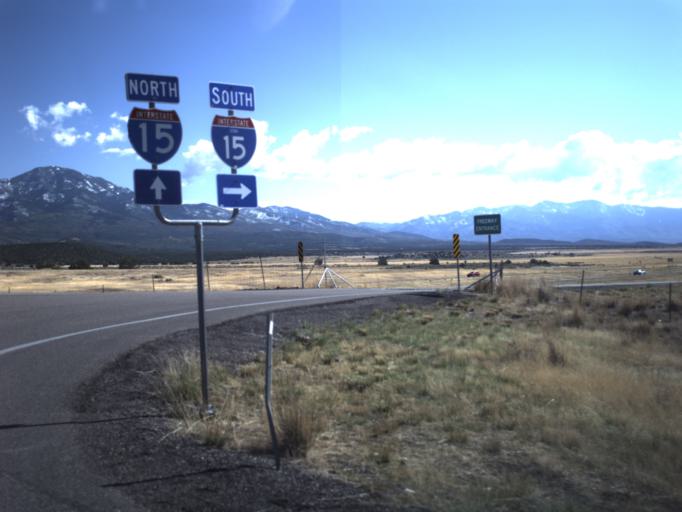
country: US
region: Utah
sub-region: Millard County
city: Fillmore
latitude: 39.0832
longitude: -112.2779
